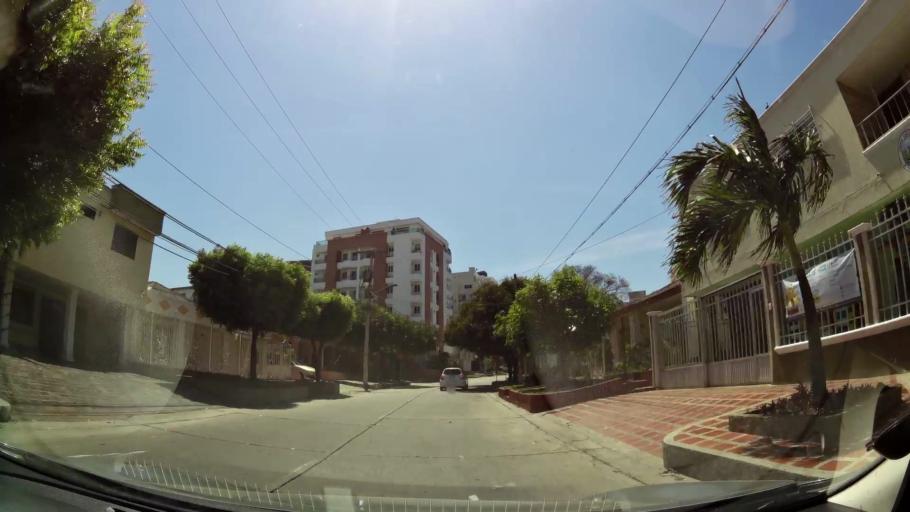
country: CO
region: Atlantico
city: Barranquilla
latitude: 10.9911
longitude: -74.8094
